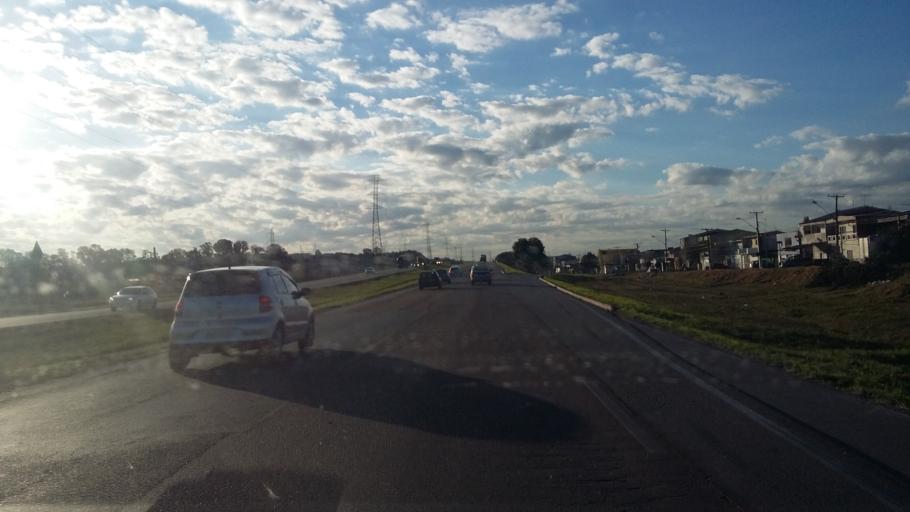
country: BR
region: Parana
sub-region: Araucaria
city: Araucaria
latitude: -25.5203
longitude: -49.3344
